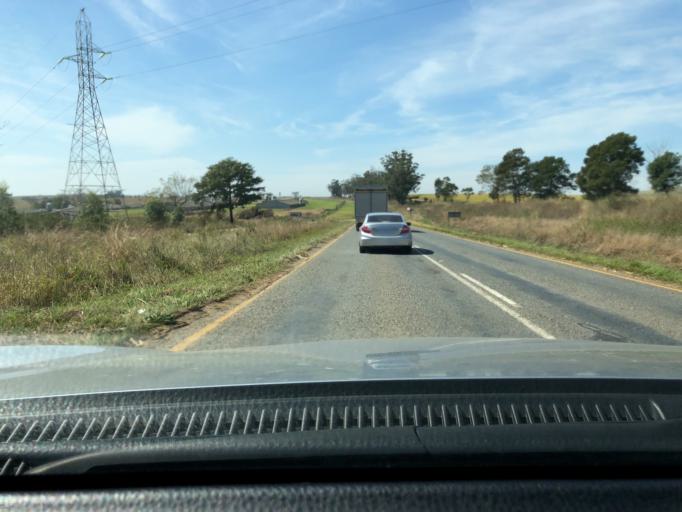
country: ZA
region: KwaZulu-Natal
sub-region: uMgungundlovu District Municipality
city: Camperdown
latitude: -29.7308
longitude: 30.4472
